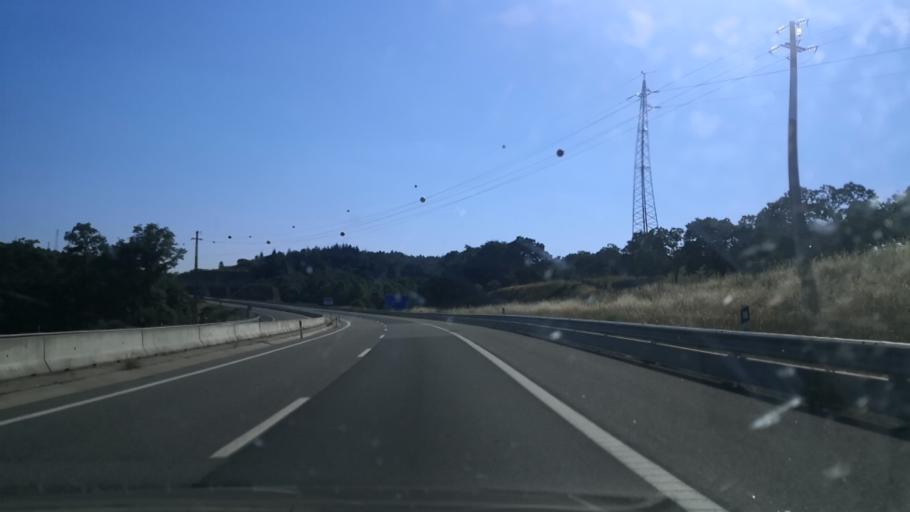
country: PT
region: Braganca
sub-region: Braganca Municipality
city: Braganca
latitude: 41.6600
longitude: -6.8252
